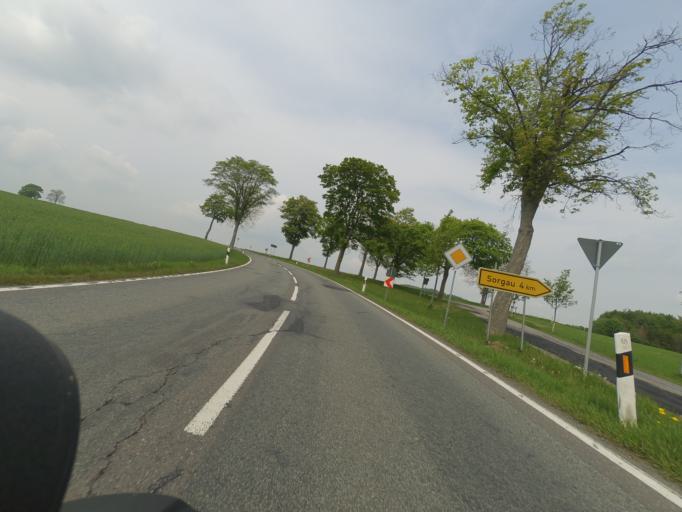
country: DE
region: Saxony
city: Zoblitz
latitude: 50.6504
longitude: 13.2791
